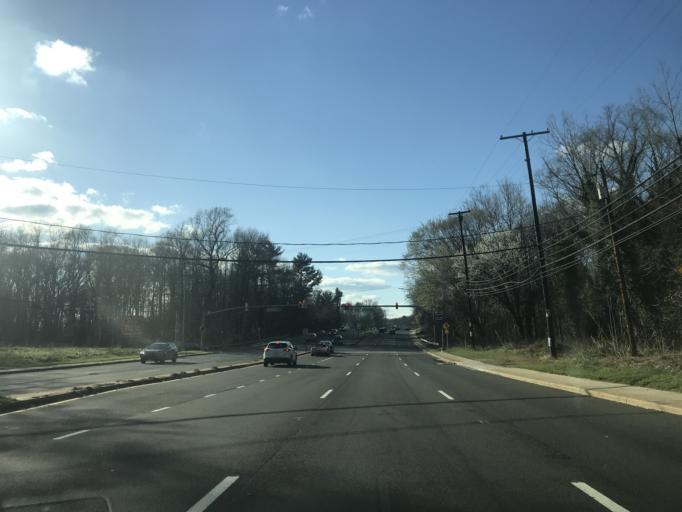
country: US
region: Maryland
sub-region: Prince George's County
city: Glenarden
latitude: 38.9203
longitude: -76.8638
